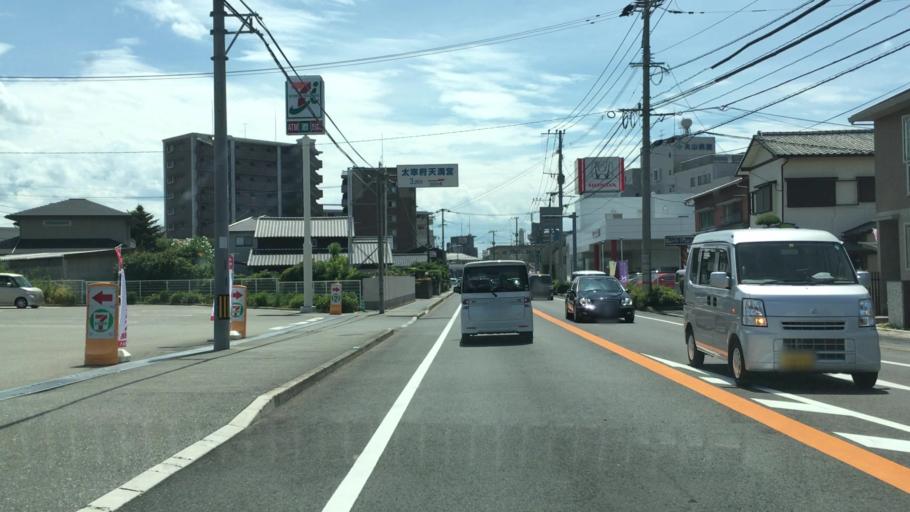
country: JP
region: Fukuoka
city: Dazaifu
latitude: 33.5153
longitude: 130.5055
